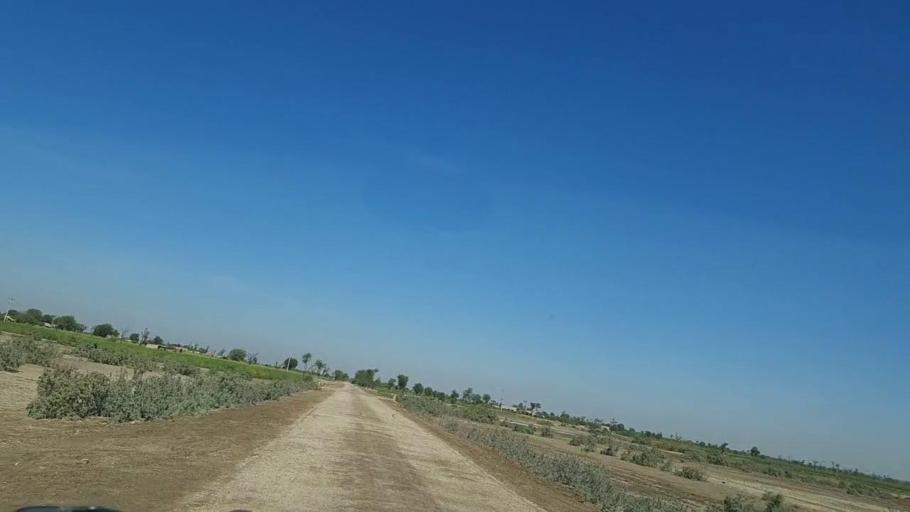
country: PK
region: Sindh
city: Dhoro Naro
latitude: 25.4975
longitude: 69.5113
